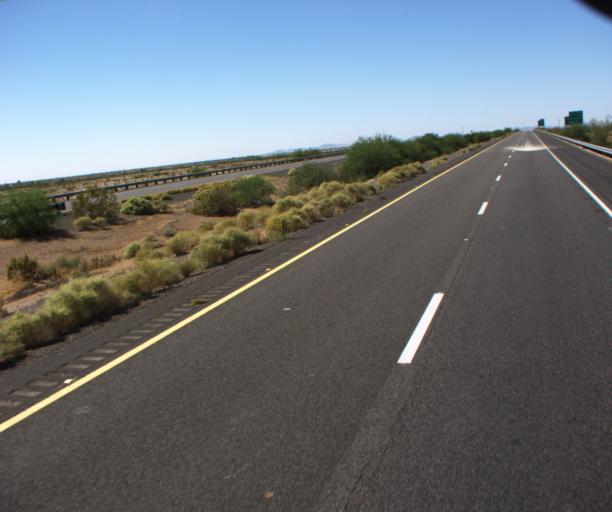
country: US
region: Arizona
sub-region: Maricopa County
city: Gila Bend
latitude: 32.9354
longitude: -112.7165
